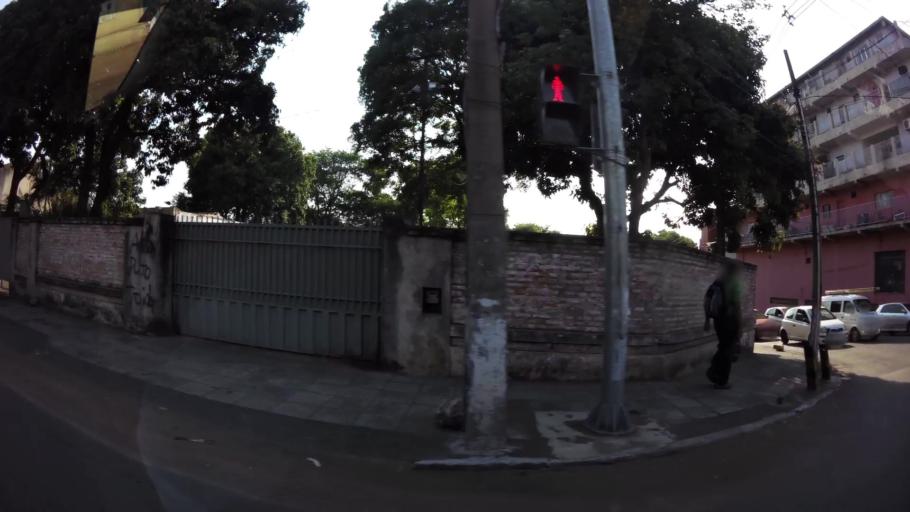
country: PY
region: Asuncion
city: Asuncion
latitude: -25.3030
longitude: -57.6203
